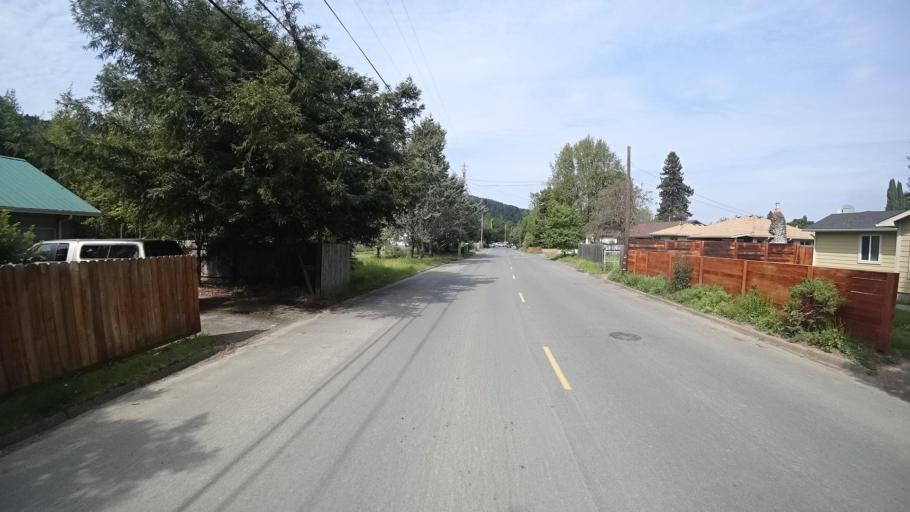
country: US
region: California
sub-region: Humboldt County
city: Redway
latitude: 40.1163
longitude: -123.8228
